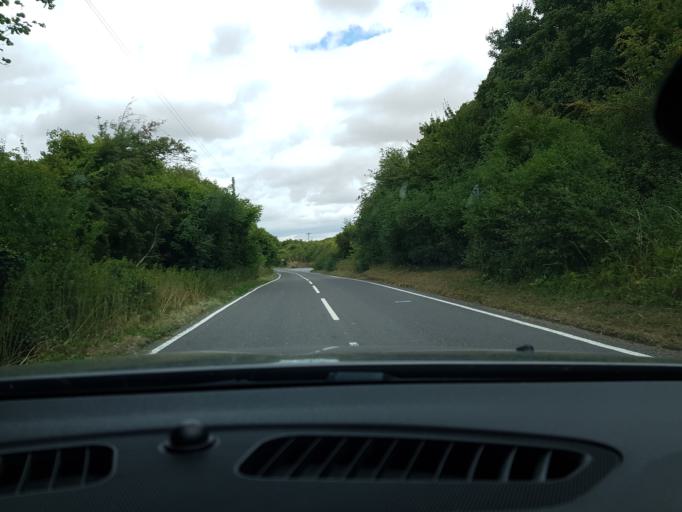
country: GB
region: England
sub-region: West Berkshire
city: Welford
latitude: 51.4956
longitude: -1.4327
